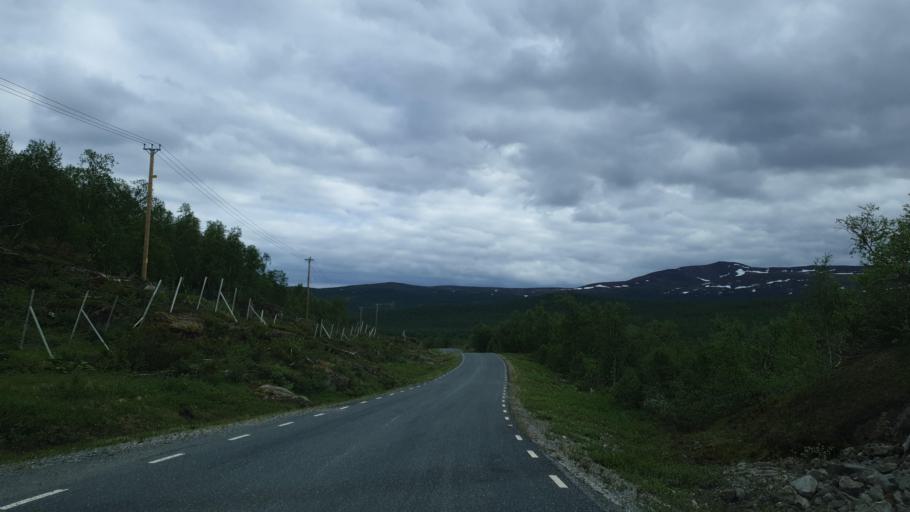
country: NO
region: Nordland
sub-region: Hattfjelldal
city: Hattfjelldal
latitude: 65.4184
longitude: 14.6825
